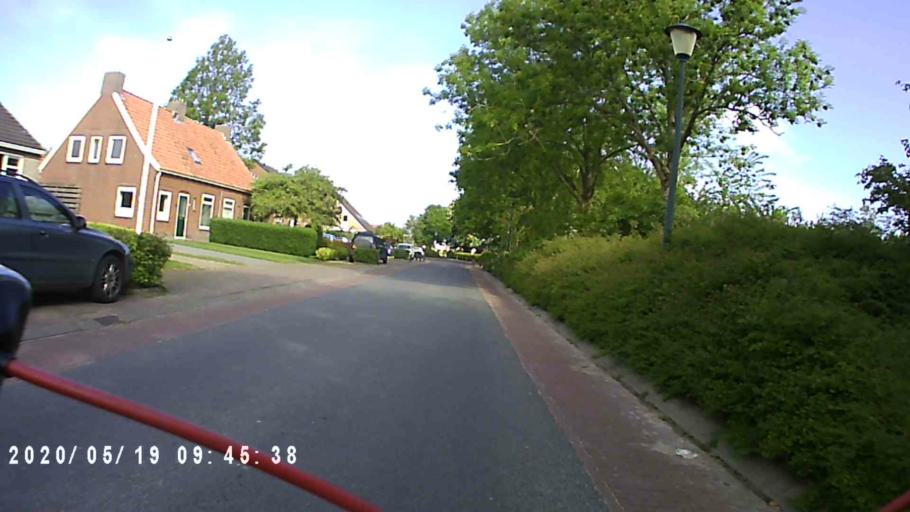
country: NL
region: Groningen
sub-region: Gemeente Zuidhorn
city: Grijpskerk
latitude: 53.2799
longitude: 6.2705
